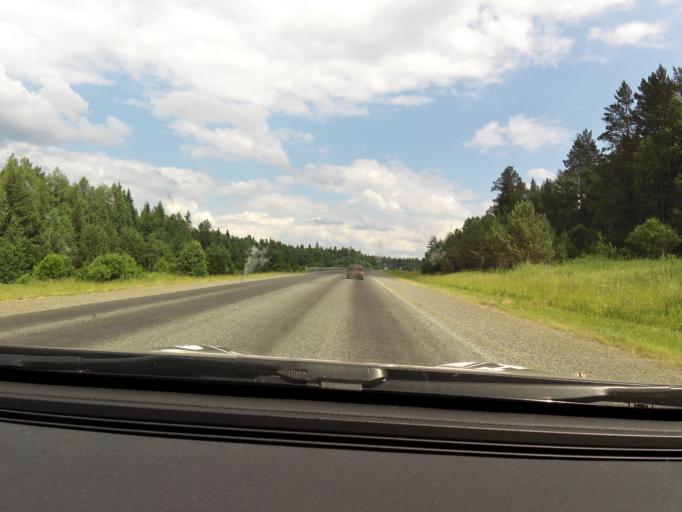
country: RU
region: Sverdlovsk
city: Arti
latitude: 56.7954
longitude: 58.4717
